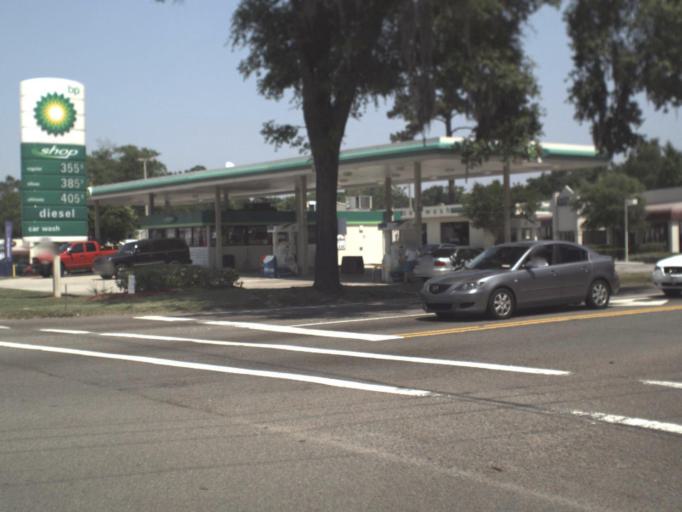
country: US
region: Florida
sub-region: Duval County
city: Jacksonville
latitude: 30.2992
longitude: -81.7674
